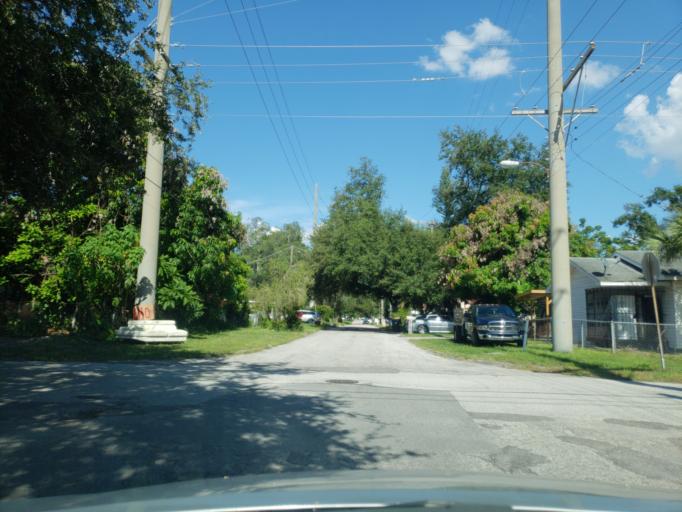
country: US
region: Florida
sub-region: Hillsborough County
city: Tampa
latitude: 27.9543
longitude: -82.4995
